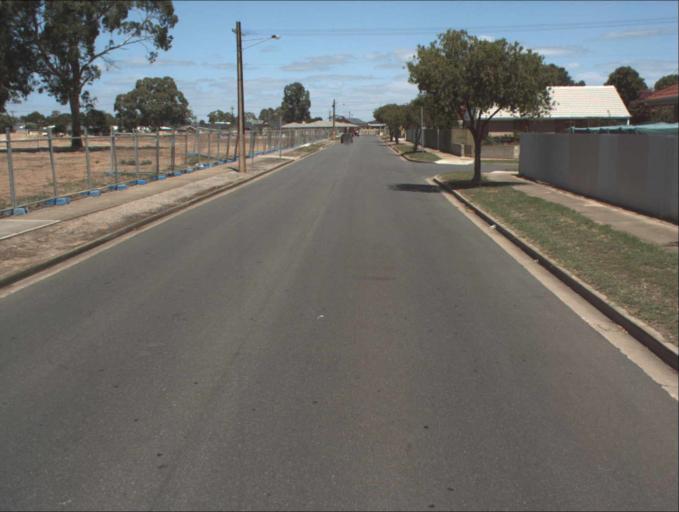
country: AU
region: South Australia
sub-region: Charles Sturt
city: Woodville North
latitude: -34.8517
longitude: 138.5541
